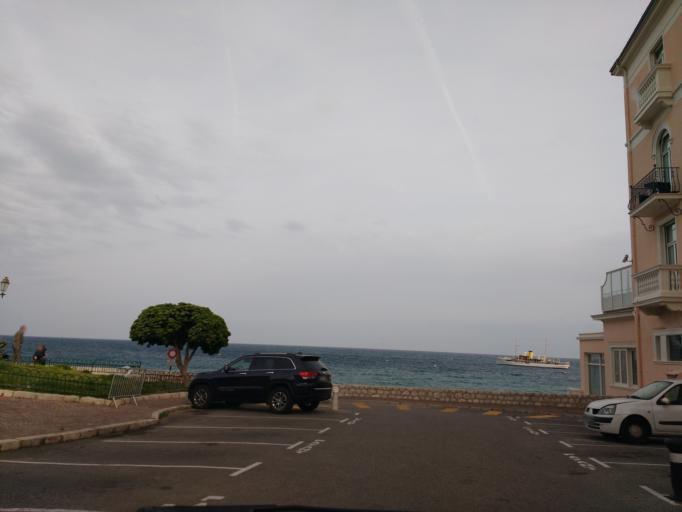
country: FR
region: Provence-Alpes-Cote d'Azur
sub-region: Departement des Alpes-Maritimes
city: Beaulieu-sur-Mer
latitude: 43.7059
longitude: 7.3356
